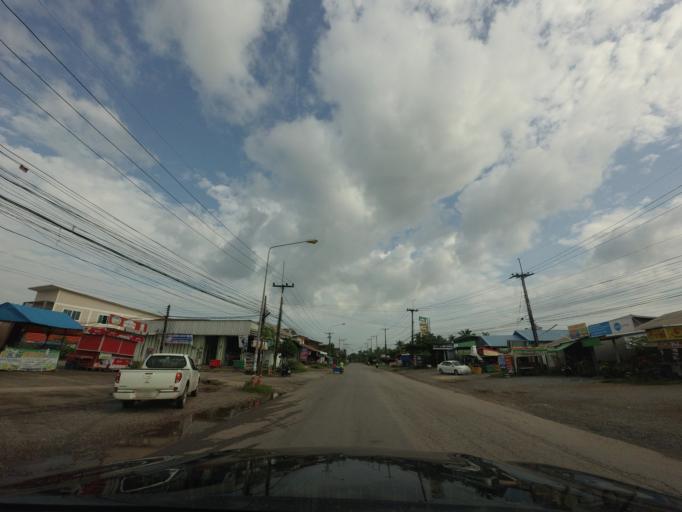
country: TH
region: Nong Khai
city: Pho Tak
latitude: 17.7768
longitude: 102.3951
